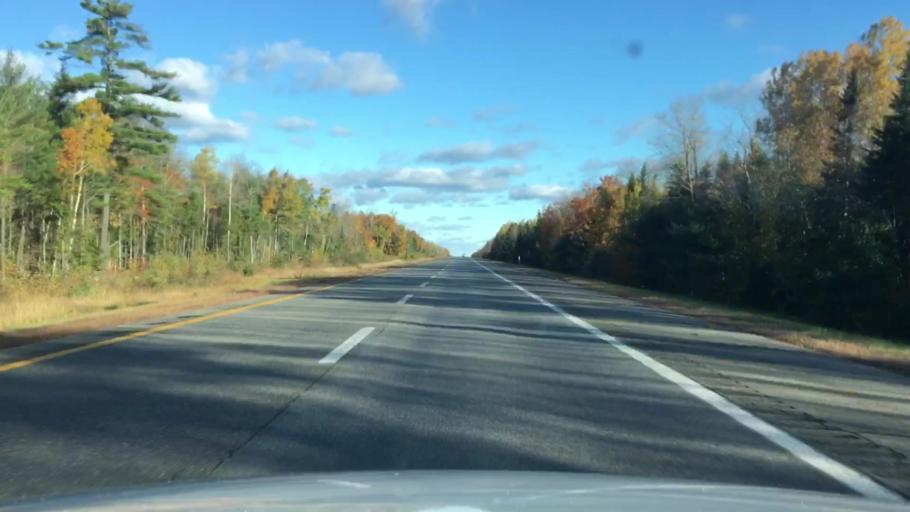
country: US
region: Maine
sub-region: Penobscot County
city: Greenbush
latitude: 45.0738
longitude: -68.6909
